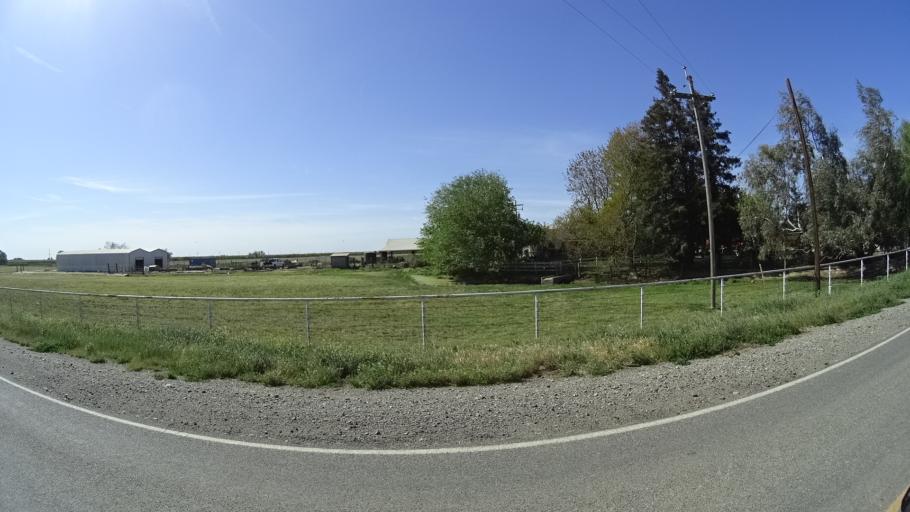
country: US
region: California
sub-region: Glenn County
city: Willows
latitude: 39.6241
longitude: -122.1796
